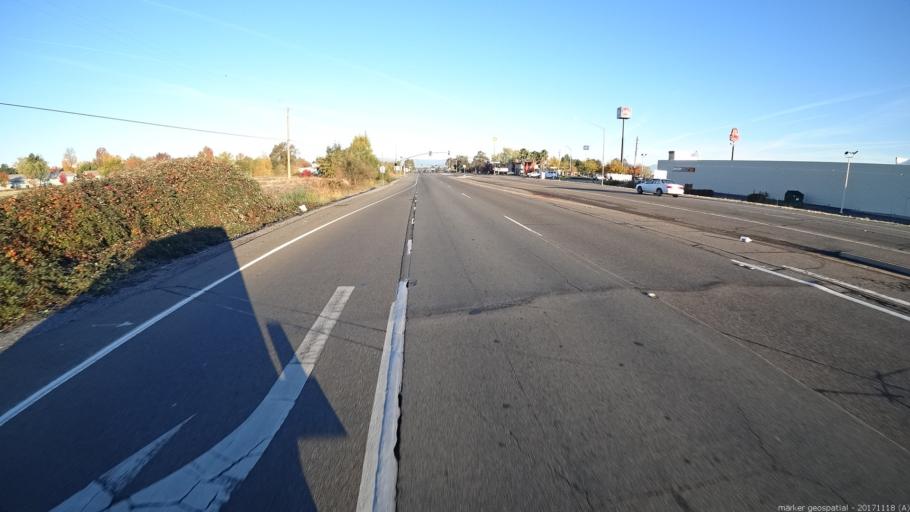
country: US
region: California
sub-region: Shasta County
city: Anderson
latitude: 40.4357
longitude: -122.2894
